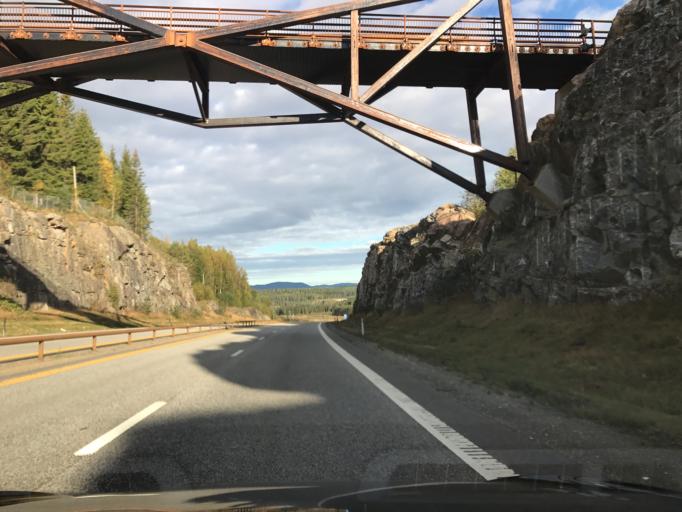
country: NO
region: Akershus
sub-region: Eidsvoll
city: Raholt
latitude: 60.2747
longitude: 11.1508
